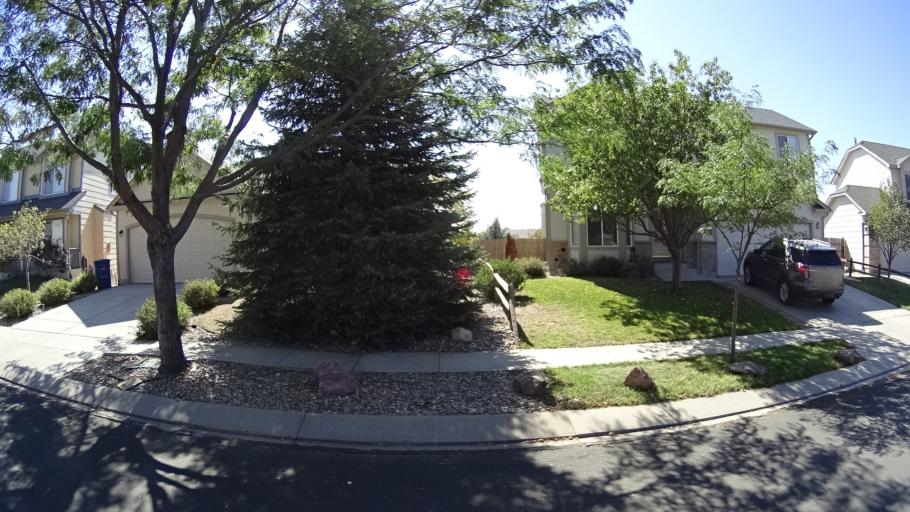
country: US
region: Colorado
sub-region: El Paso County
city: Cimarron Hills
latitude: 38.8873
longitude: -104.6930
